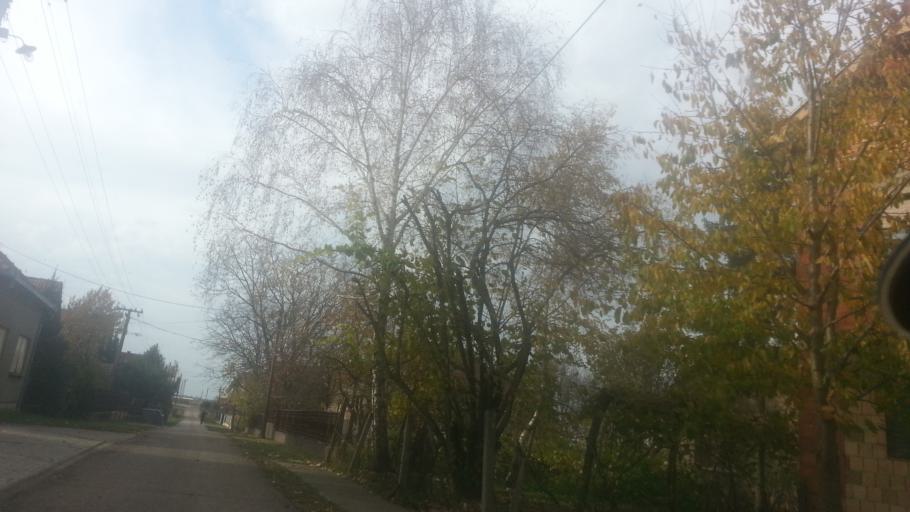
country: RS
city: Putinci
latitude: 44.9966
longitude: 19.9665
